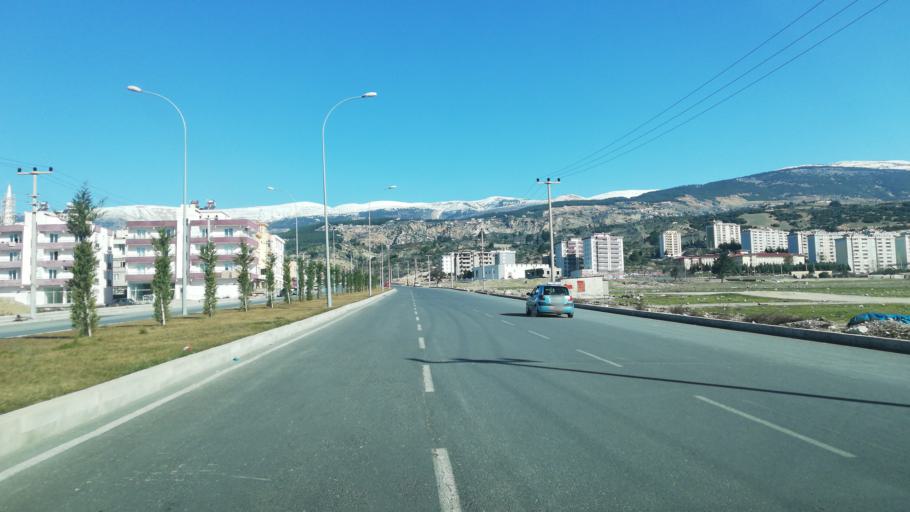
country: TR
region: Kahramanmaras
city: Kahramanmaras
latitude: 37.5788
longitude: 36.9746
